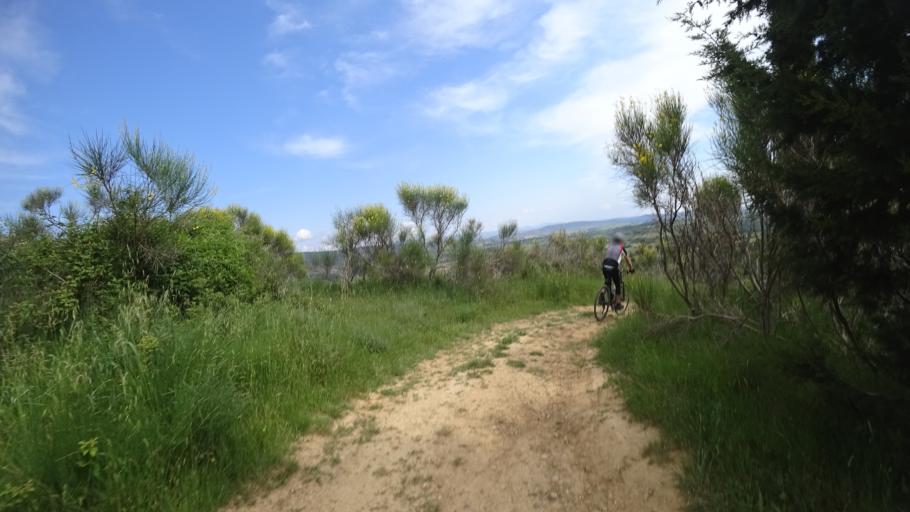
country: FR
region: Languedoc-Roussillon
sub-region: Departement de l'Aude
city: Canet
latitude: 43.2591
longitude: 2.8085
